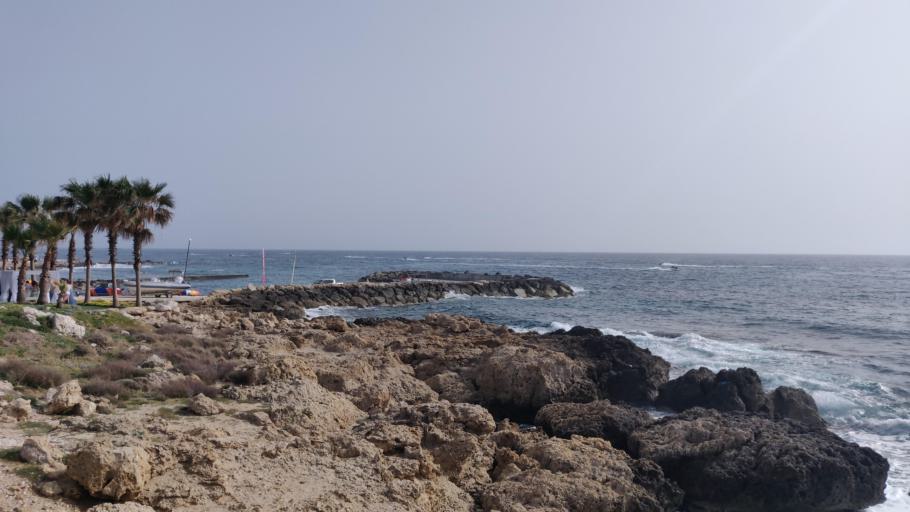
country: CY
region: Pafos
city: Paphos
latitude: 34.7466
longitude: 32.4233
